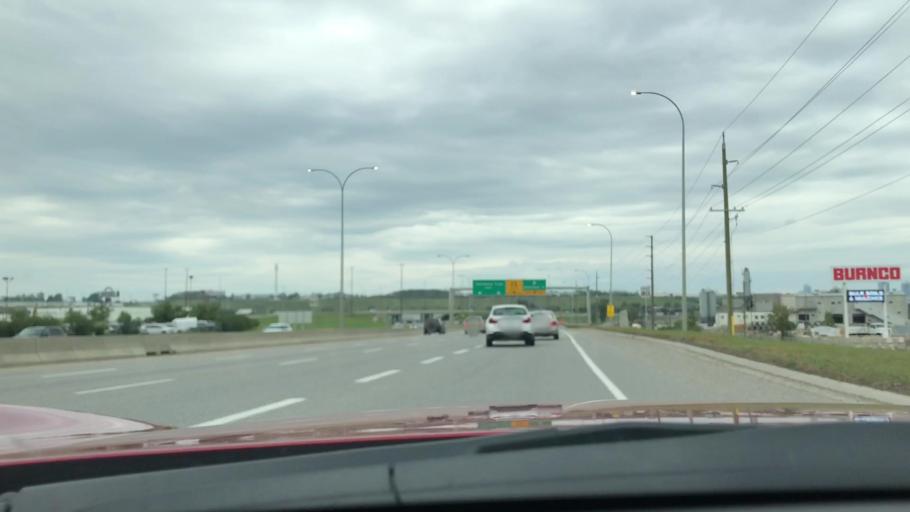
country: CA
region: Alberta
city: Calgary
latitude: 50.9895
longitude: -114.0279
